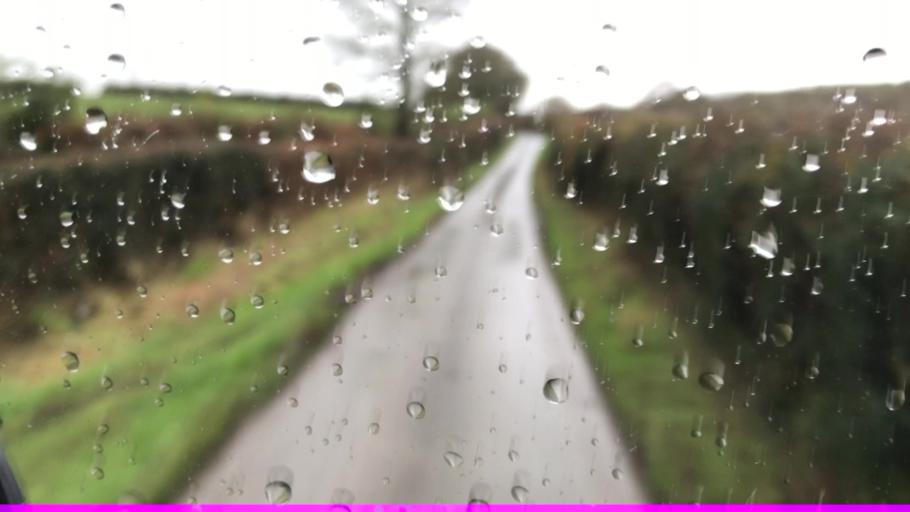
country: GB
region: England
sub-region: Devon
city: Chudleigh
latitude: 50.6360
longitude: -3.6143
